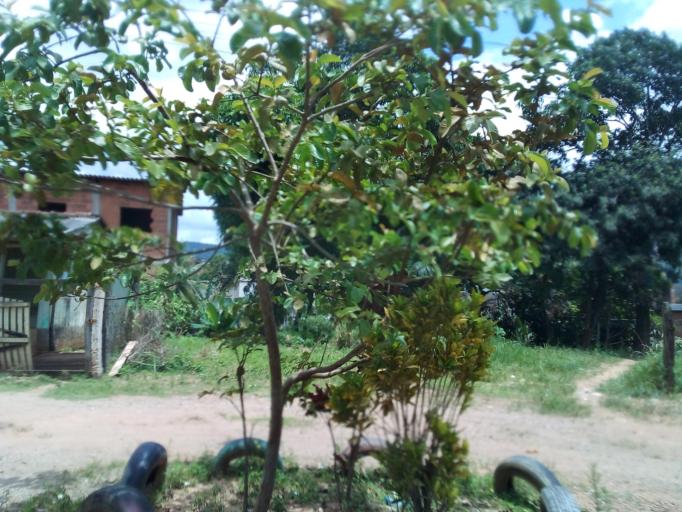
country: BR
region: Espirito Santo
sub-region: Fundao
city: Fundao
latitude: -19.9310
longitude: -40.4010
